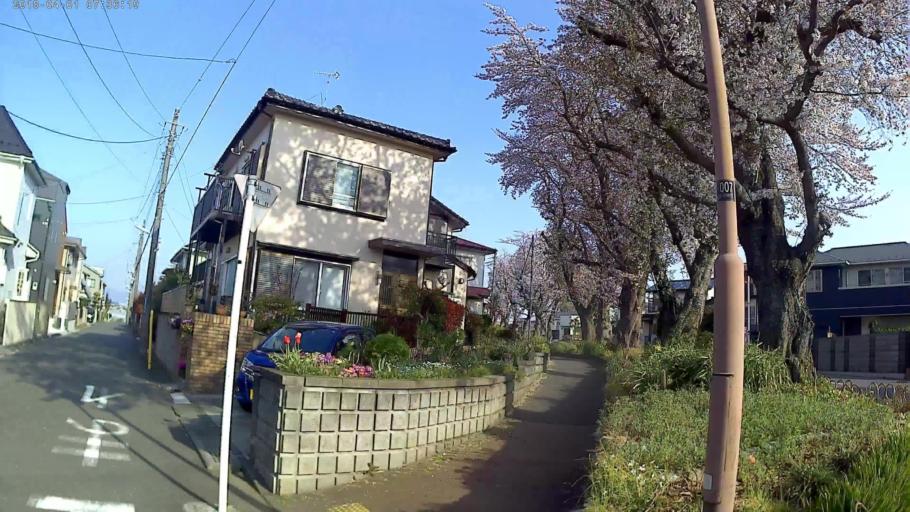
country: JP
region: Kanagawa
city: Atsugi
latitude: 35.4348
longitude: 139.4090
